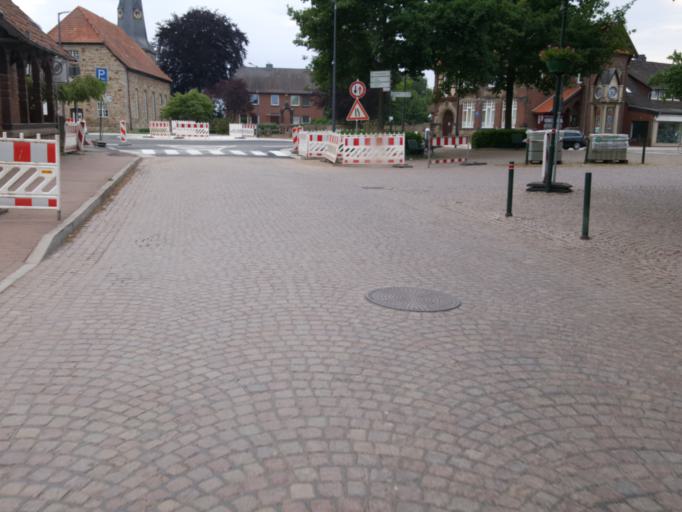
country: DE
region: Lower Saxony
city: Rehburg-Loccum
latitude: 52.4747
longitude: 9.2302
